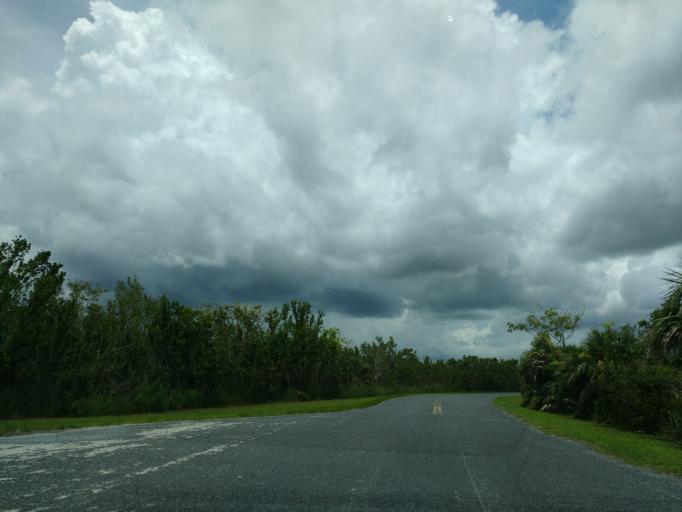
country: US
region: Florida
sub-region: Miami-Dade County
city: Florida City
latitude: 25.2826
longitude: -80.7997
